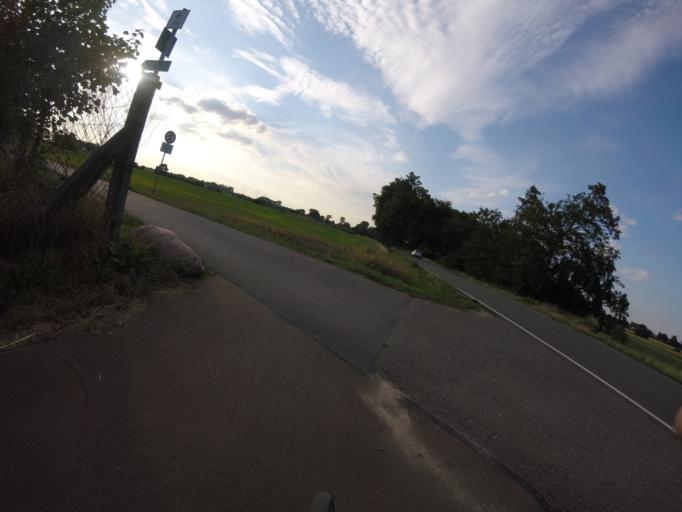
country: DE
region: Brandenburg
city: Altlandsberg
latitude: 52.5738
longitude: 13.7151
